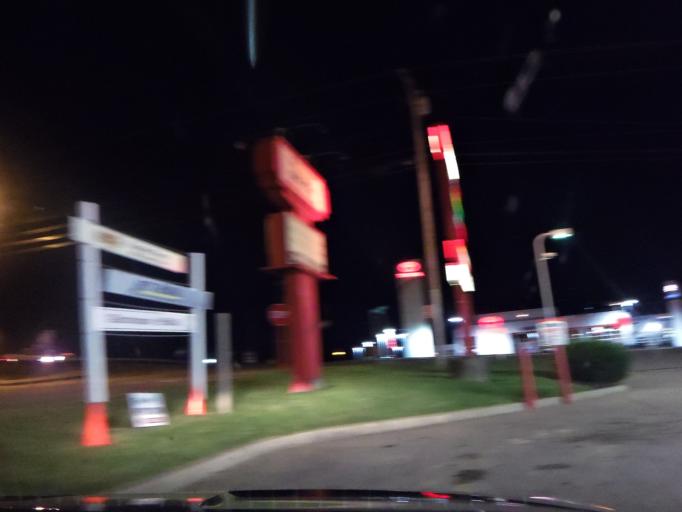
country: US
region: Kentucky
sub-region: Grant County
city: Dry Ridge
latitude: 38.6834
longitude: -84.6034
